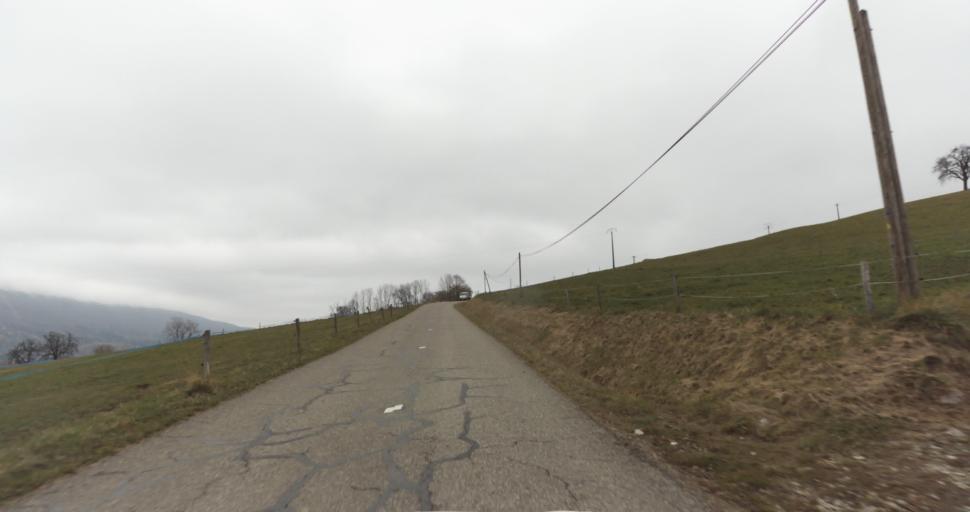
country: FR
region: Rhone-Alpes
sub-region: Departement de la Haute-Savoie
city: Saint-Jorioz
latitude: 45.8011
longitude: 6.1576
